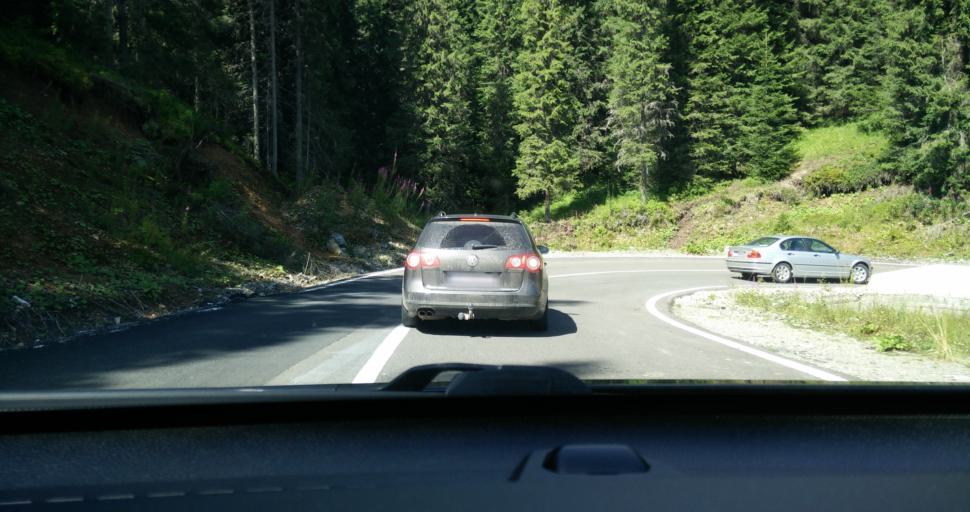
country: RO
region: Hunedoara
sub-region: Oras Petrila
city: Petrila
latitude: 45.5056
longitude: 23.6471
